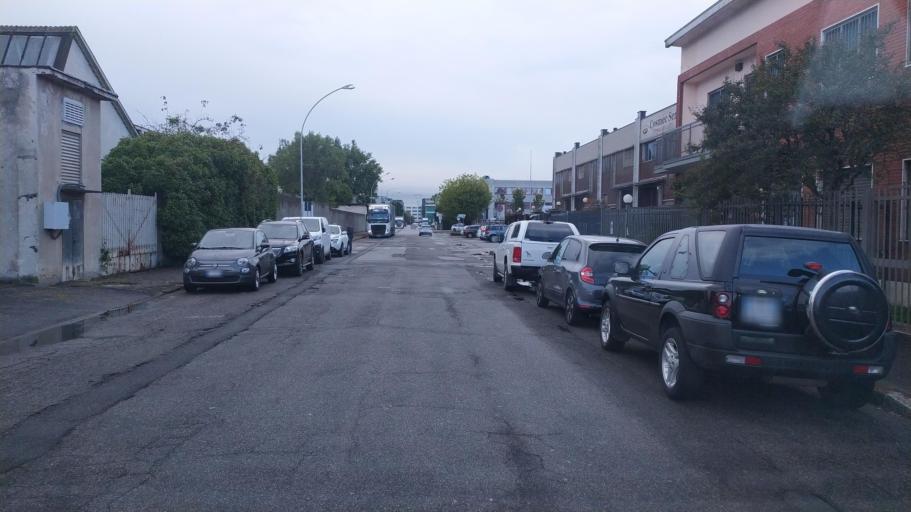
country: IT
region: Lombardy
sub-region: Citta metropolitana di Milano
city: Trezzano sul Naviglio
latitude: 45.4313
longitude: 9.0681
